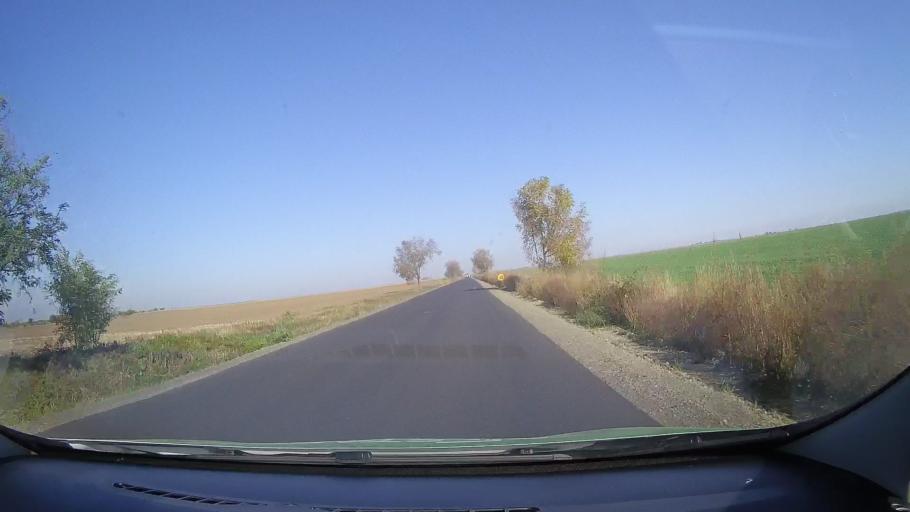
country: RO
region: Satu Mare
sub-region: Comuna Tiream
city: Tiream
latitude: 47.6251
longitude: 22.4679
